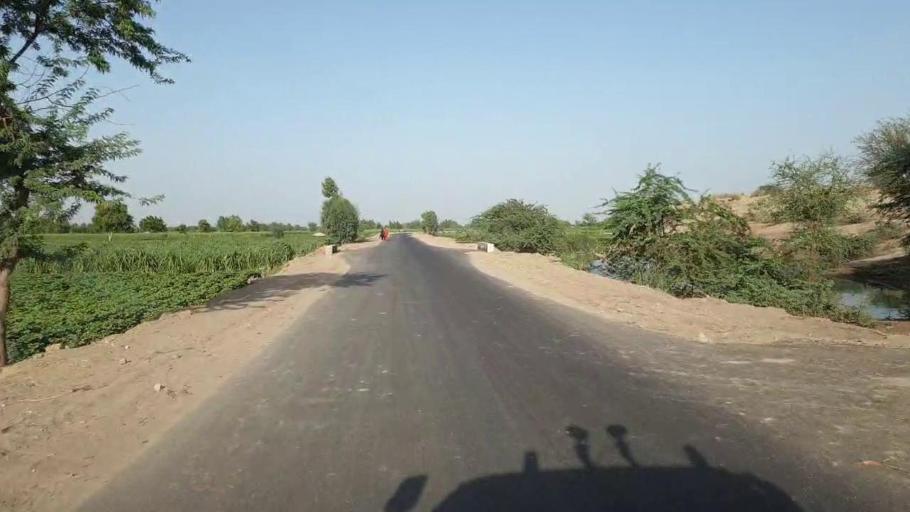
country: PK
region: Sindh
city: Jam Sahib
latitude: 26.3486
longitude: 68.5642
